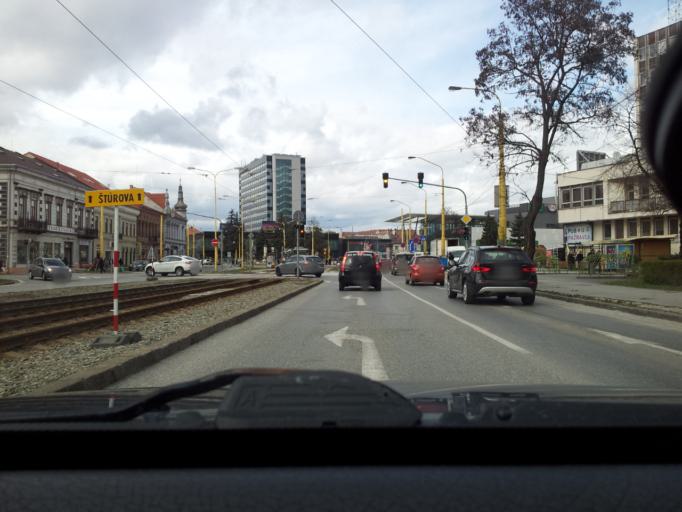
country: SK
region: Kosicky
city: Kosice
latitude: 48.7151
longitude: 21.2611
